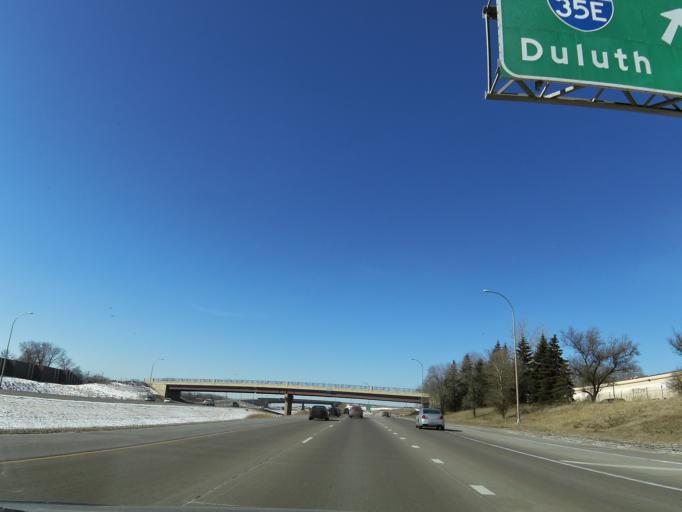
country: US
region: Minnesota
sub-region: Ramsey County
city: Vadnais Heights
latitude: 45.0379
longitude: -93.0552
